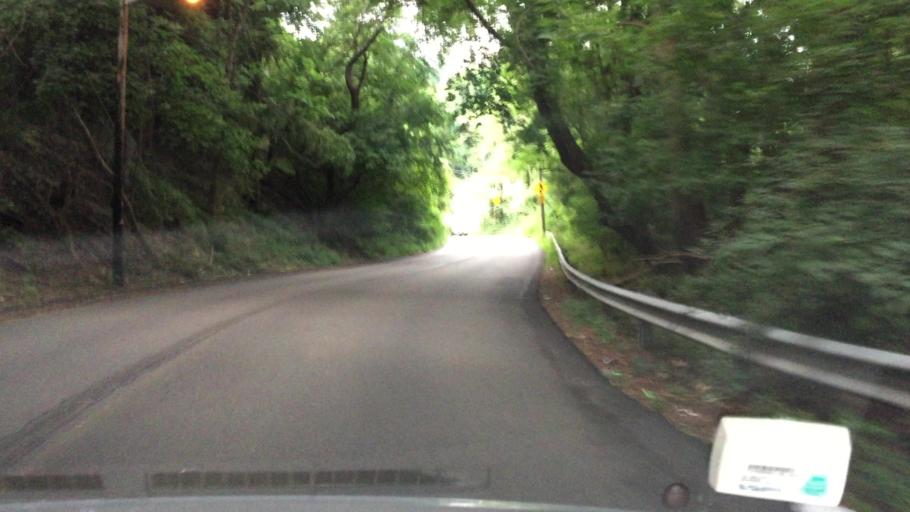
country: US
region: Pennsylvania
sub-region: Allegheny County
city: Pittsburgh
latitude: 40.4289
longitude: -80.0047
